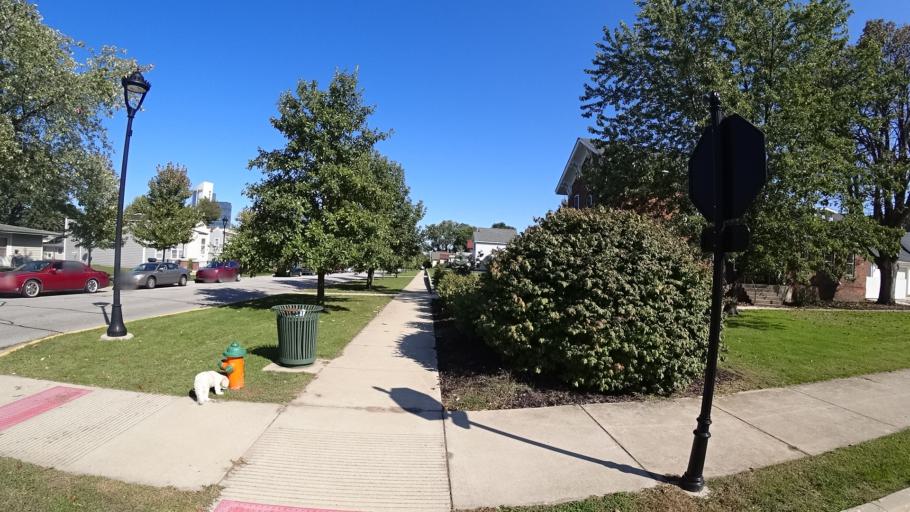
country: US
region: Indiana
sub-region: LaPorte County
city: Michigan City
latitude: 41.7161
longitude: -86.8965
